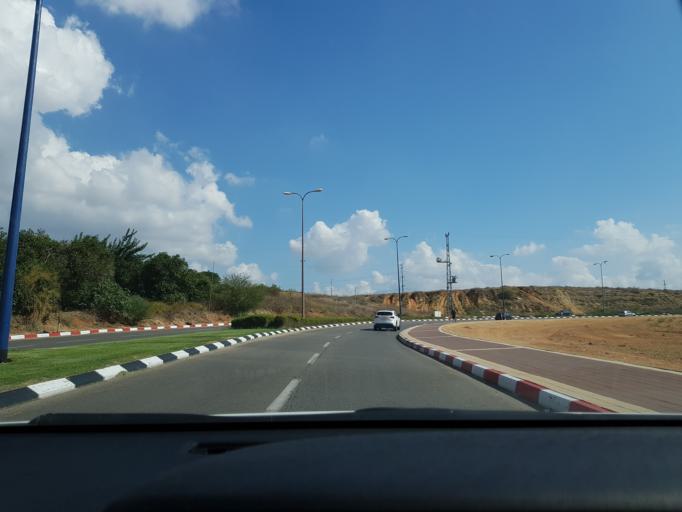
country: IL
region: Central District
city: Ness Ziona
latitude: 31.9155
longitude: 34.8155
